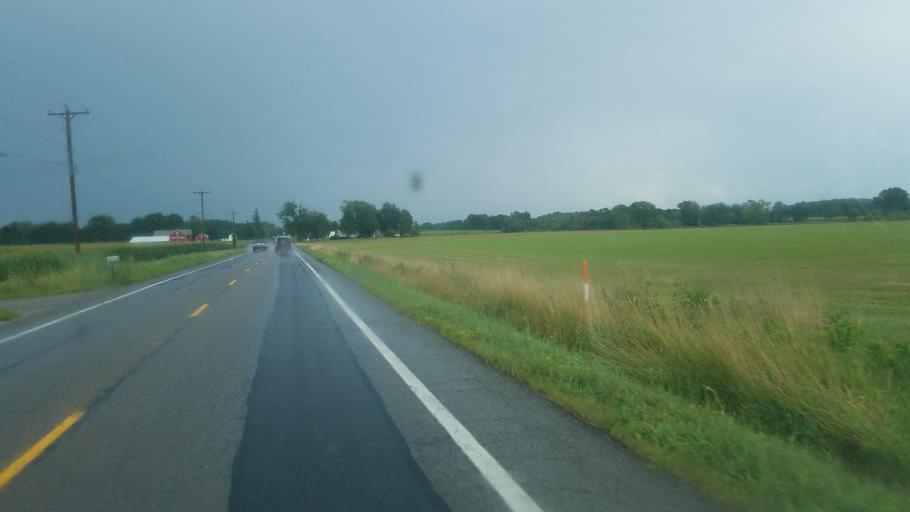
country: US
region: Ohio
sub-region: Ashtabula County
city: Orwell
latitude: 41.4617
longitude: -80.8907
